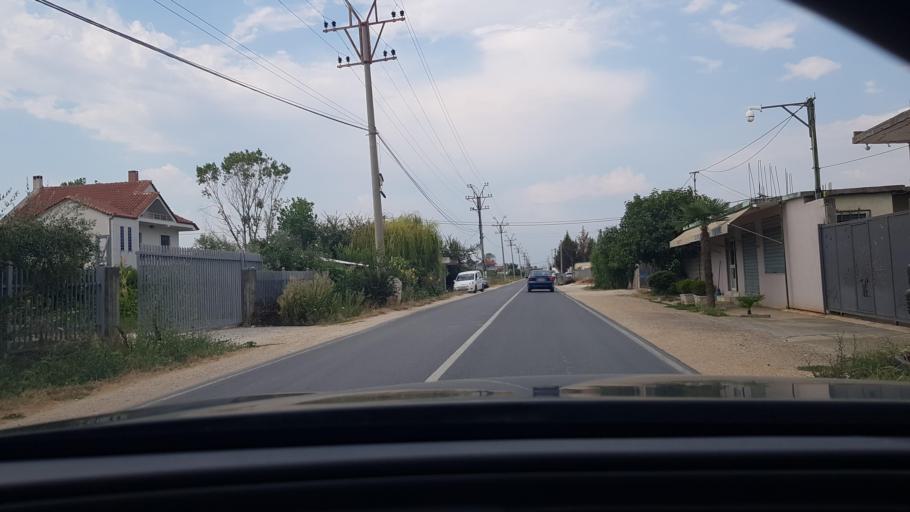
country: AL
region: Durres
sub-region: Rrethi i Durresit
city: Sukth
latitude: 41.4067
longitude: 19.5468
